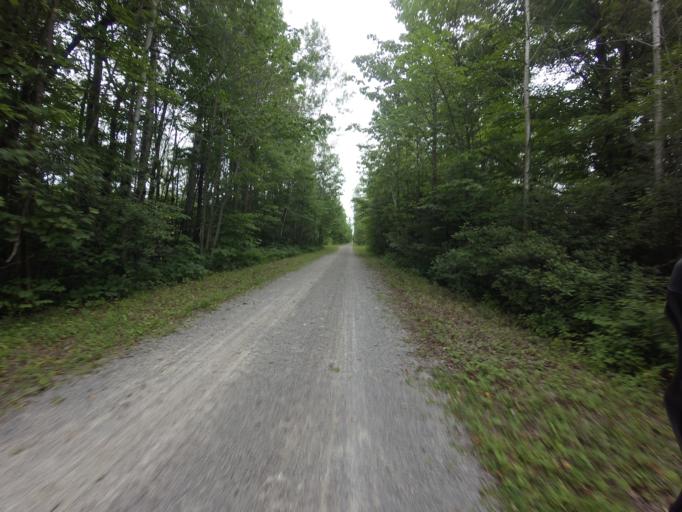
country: CA
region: Ontario
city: Ottawa
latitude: 45.2224
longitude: -75.6216
